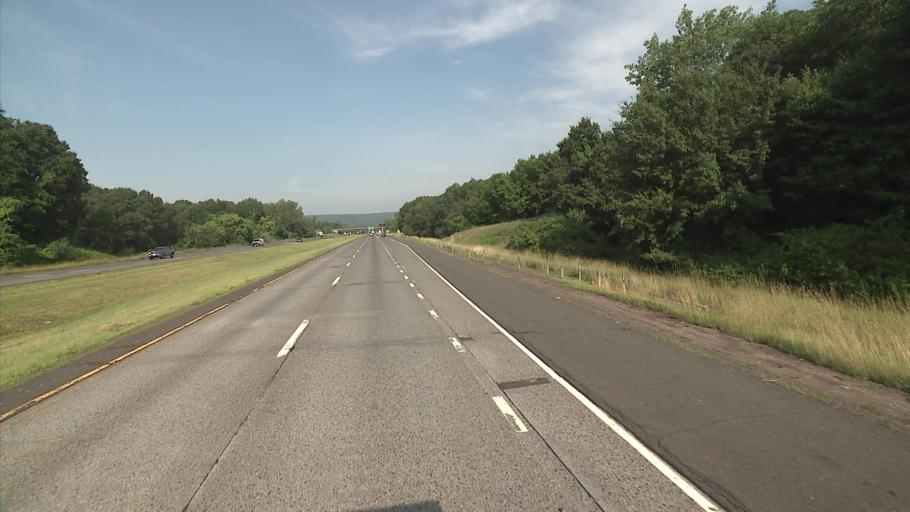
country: US
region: Connecticut
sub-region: New Haven County
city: Cheshire Village
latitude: 41.5565
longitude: -72.8833
